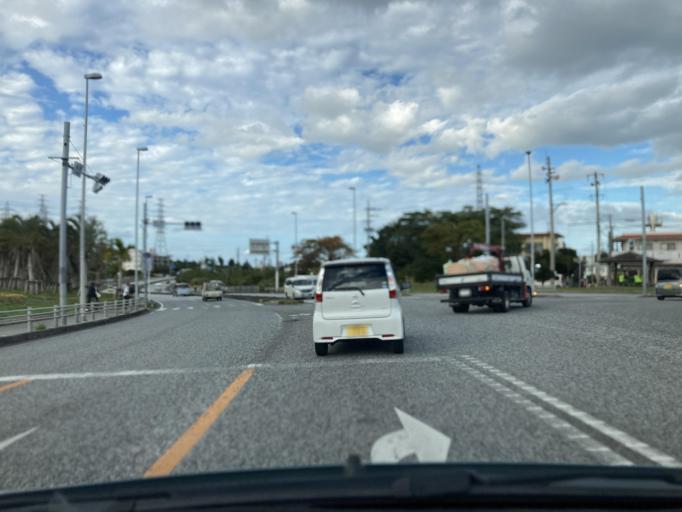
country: JP
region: Okinawa
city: Ishikawa
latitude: 26.3879
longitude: 127.8286
